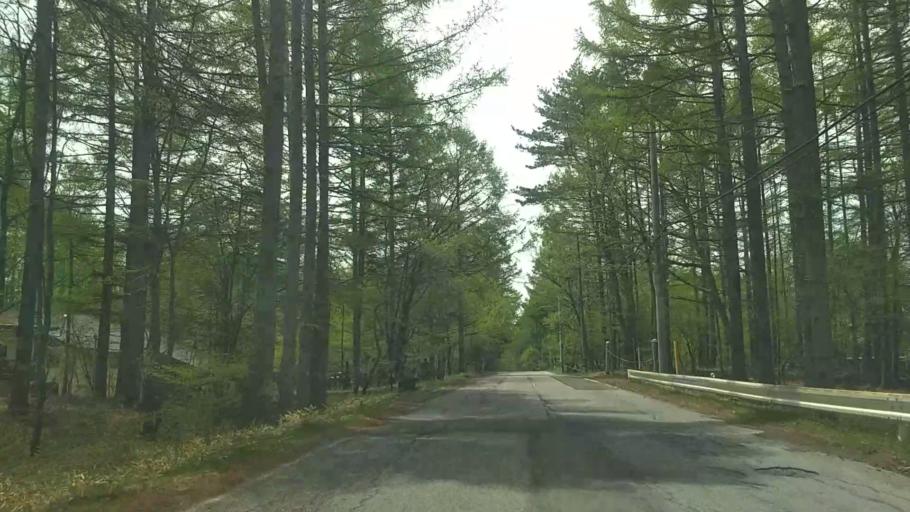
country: JP
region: Nagano
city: Chino
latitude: 36.0450
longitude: 138.2987
